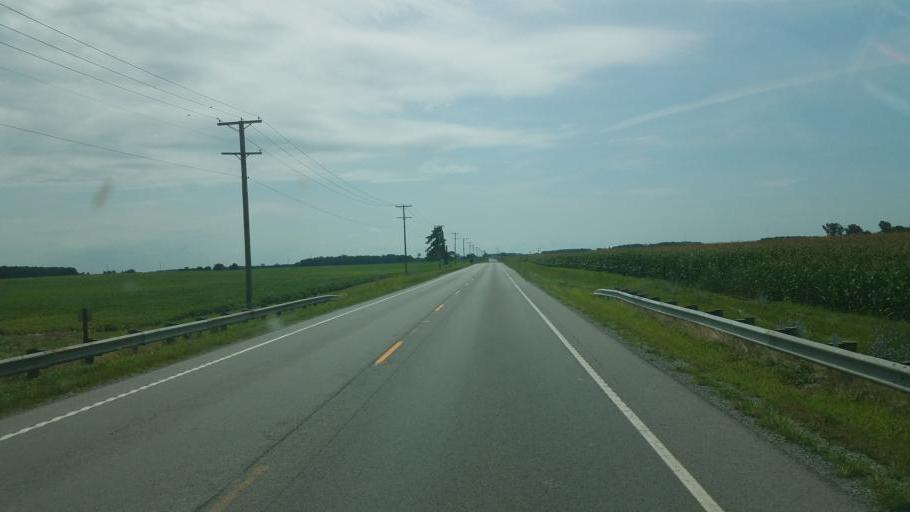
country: US
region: Ohio
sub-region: Wyandot County
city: Upper Sandusky
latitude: 40.8722
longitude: -83.3155
